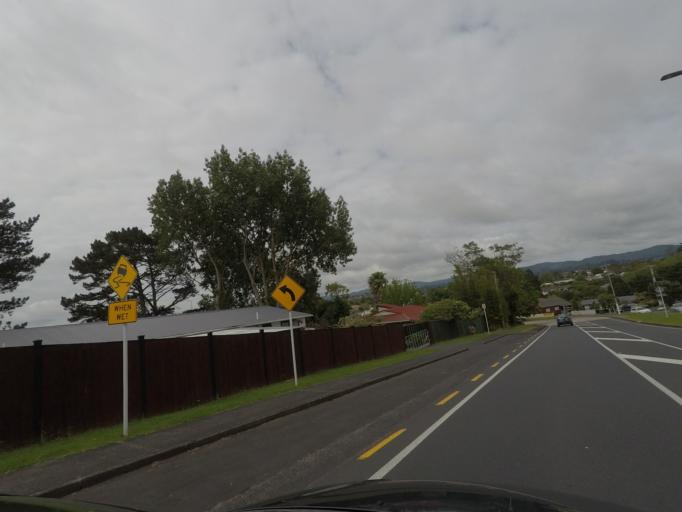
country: NZ
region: Auckland
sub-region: Auckland
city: Rosebank
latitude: -36.8568
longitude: 174.6106
